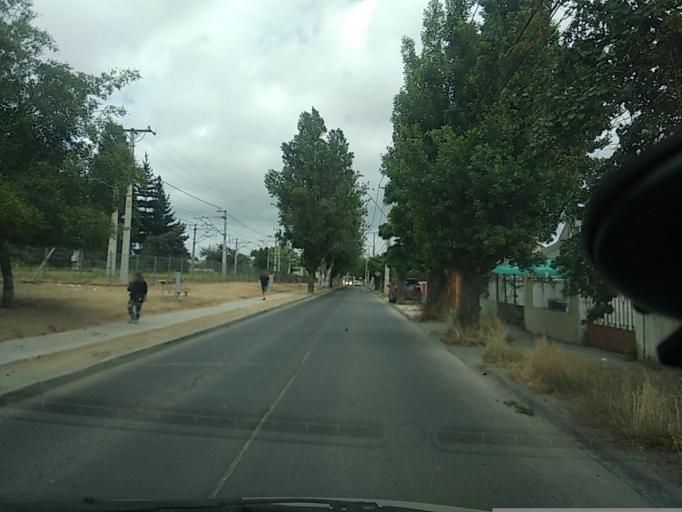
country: CL
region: Valparaiso
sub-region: Provincia de Marga Marga
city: Villa Alemana
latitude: -33.0419
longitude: -71.3669
